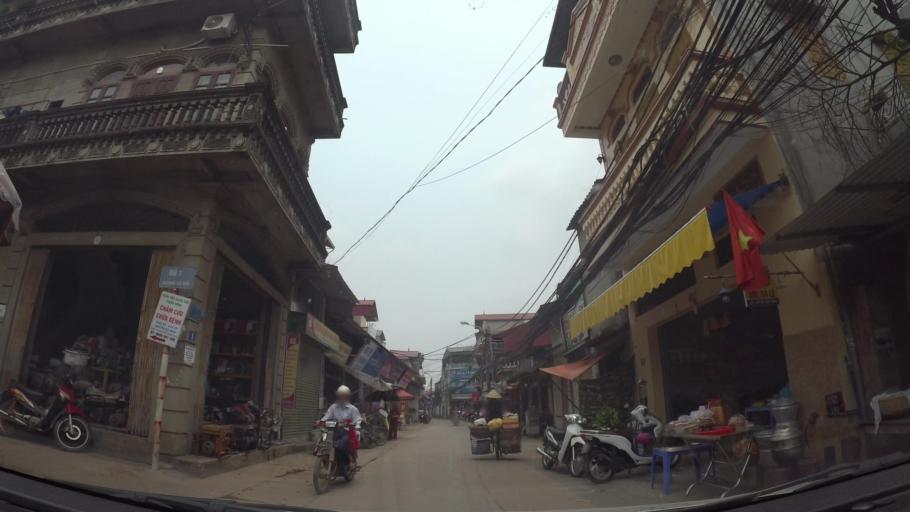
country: VN
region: Ha Noi
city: Ha Dong
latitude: 20.9785
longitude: 105.7464
